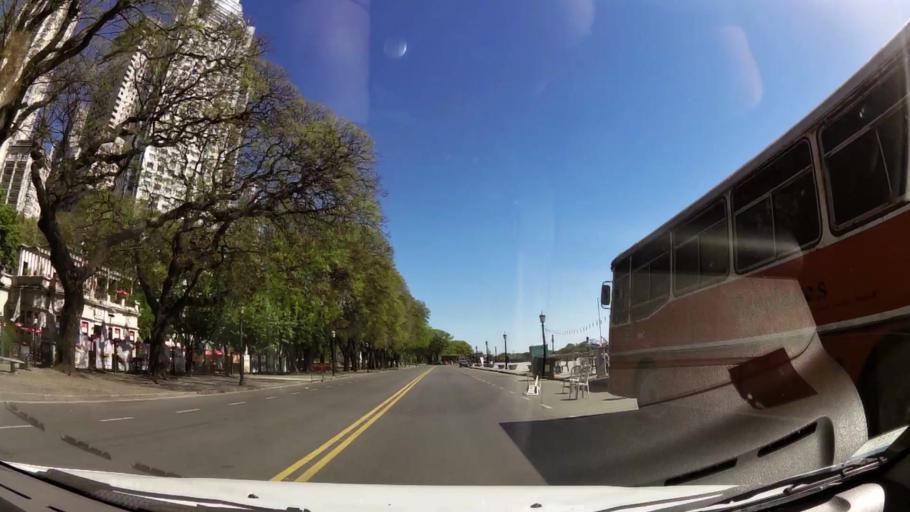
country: AR
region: Buenos Aires F.D.
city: Buenos Aires
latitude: -34.6133
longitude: -58.3579
